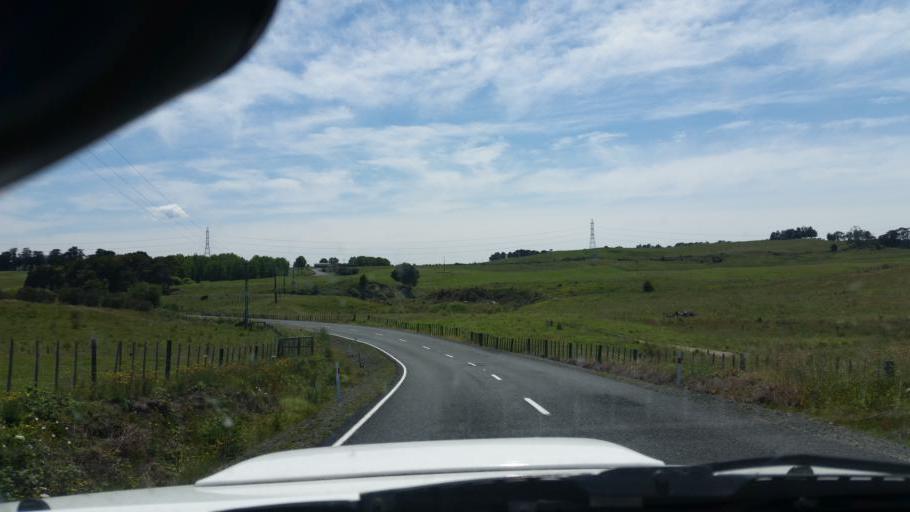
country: NZ
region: Auckland
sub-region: Auckland
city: Wellsford
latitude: -36.1693
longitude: 174.4216
